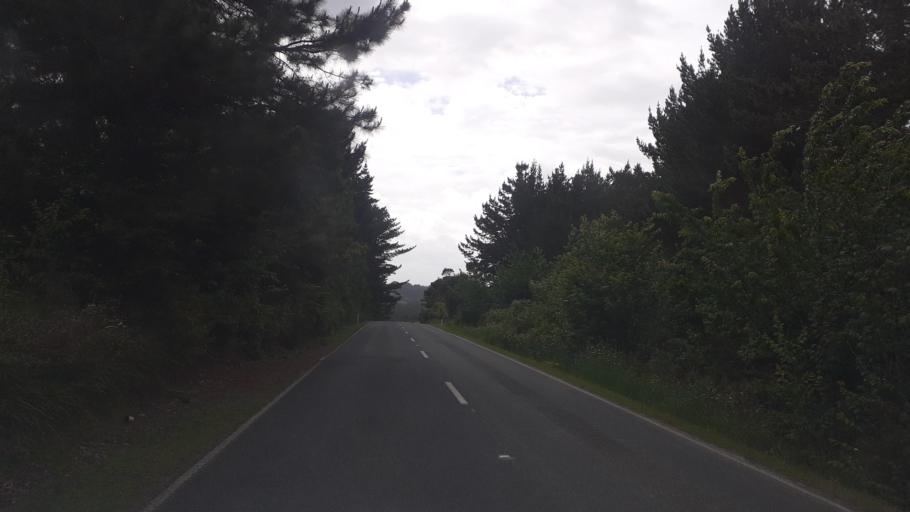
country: NZ
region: Northland
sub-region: Far North District
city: Kerikeri
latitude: -35.2243
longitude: 173.9996
